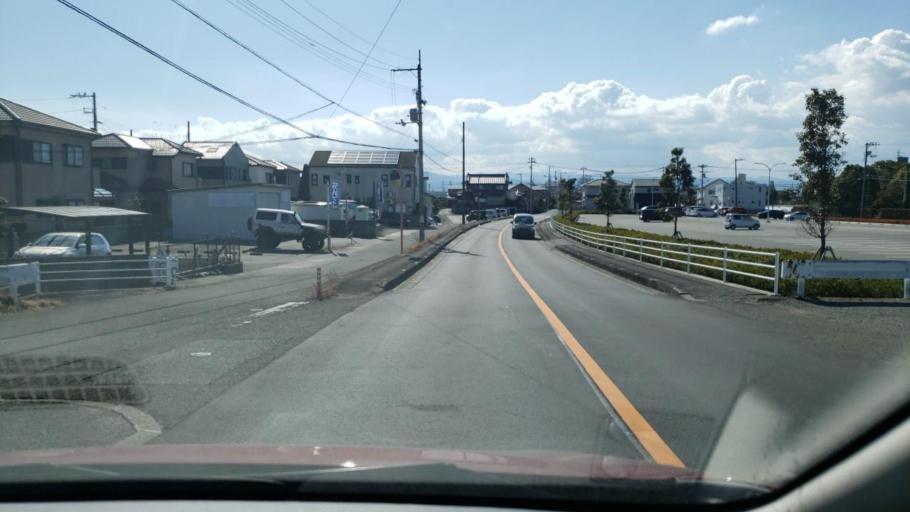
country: JP
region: Tokushima
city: Tokushima-shi
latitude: 34.1337
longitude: 134.5277
